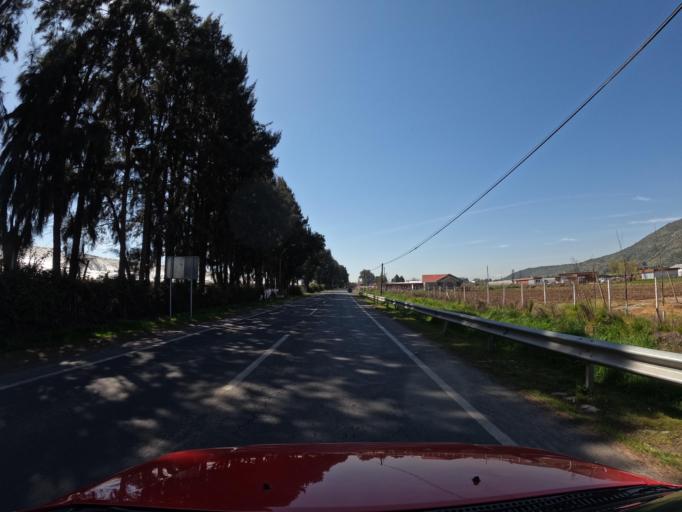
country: CL
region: Maule
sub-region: Provincia de Curico
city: Rauco
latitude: -35.0088
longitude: -71.4122
